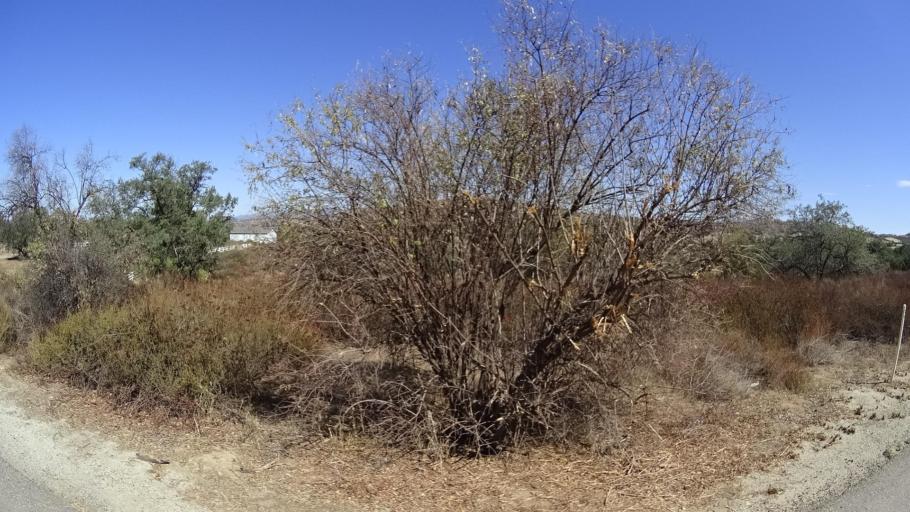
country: US
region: California
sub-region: San Diego County
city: Ramona
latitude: 33.0376
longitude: -116.8322
